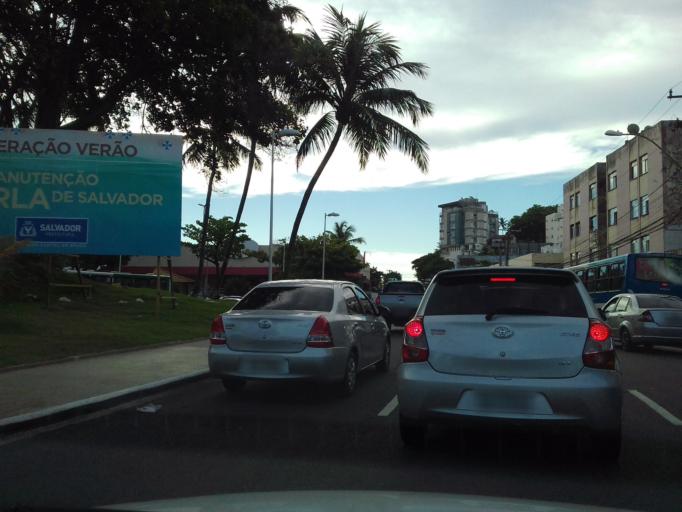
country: BR
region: Bahia
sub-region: Salvador
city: Salvador
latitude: -13.0122
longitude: -38.4816
